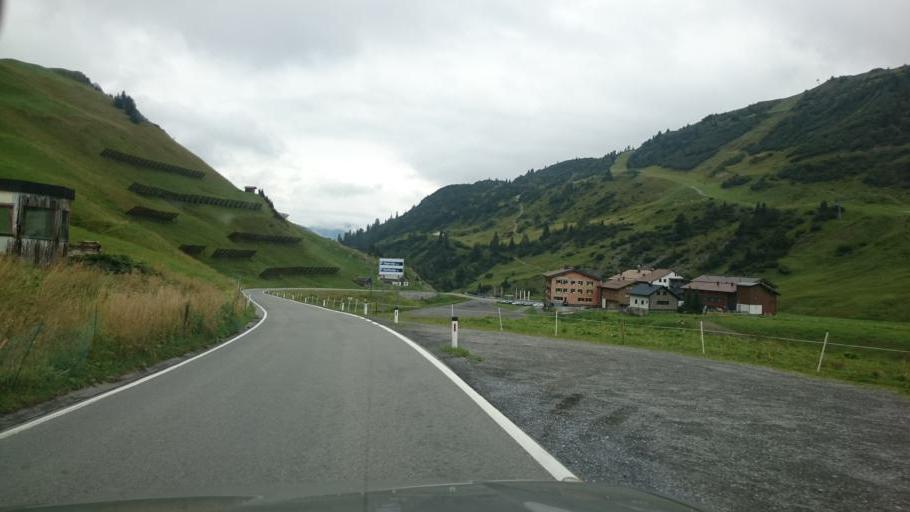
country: AT
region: Vorarlberg
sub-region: Politischer Bezirk Bregenz
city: Warth
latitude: 47.2690
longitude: 10.1454
